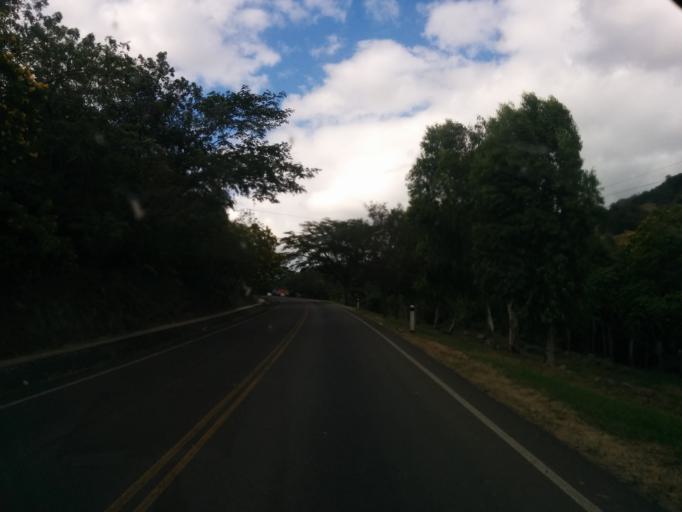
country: NI
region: Esteli
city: Esteli
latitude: 13.0078
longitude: -86.3090
